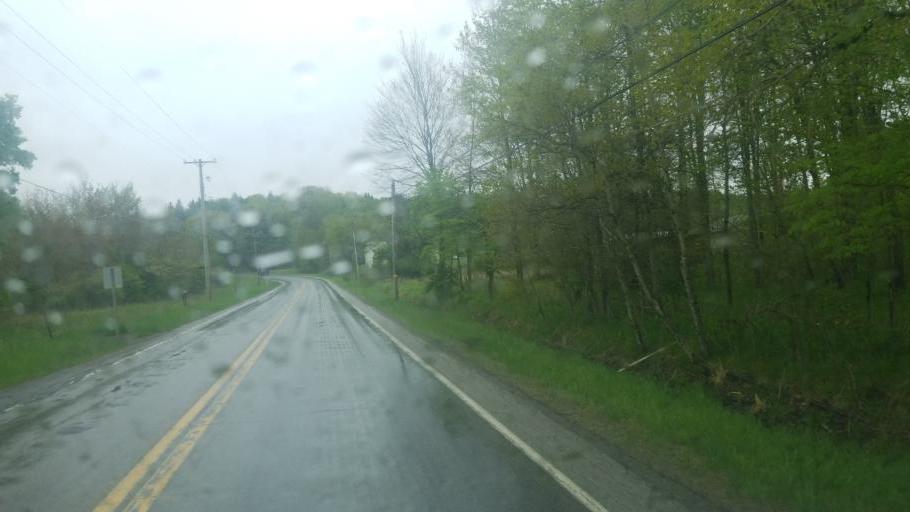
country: US
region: Pennsylvania
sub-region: Forest County
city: Tionesta
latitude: 41.3885
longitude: -79.3219
